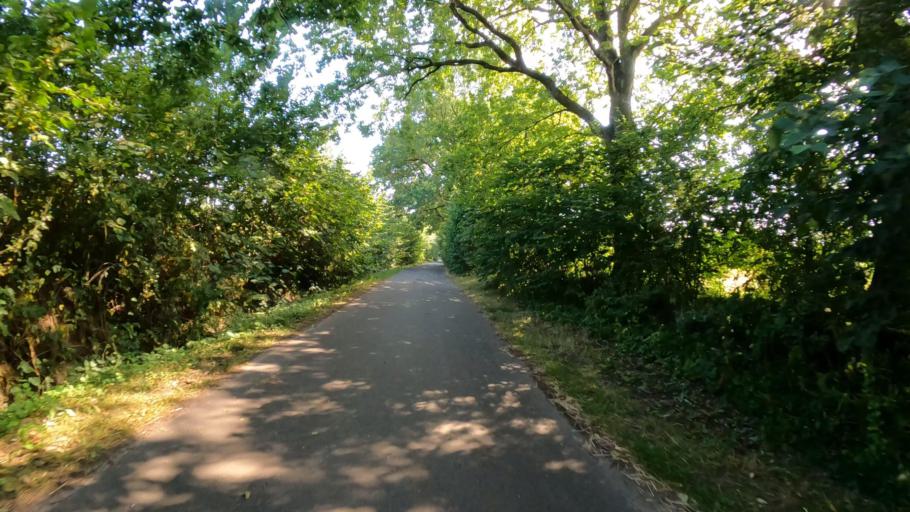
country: DE
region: Schleswig-Holstein
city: Norderstedt
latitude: 53.6676
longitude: 9.9654
